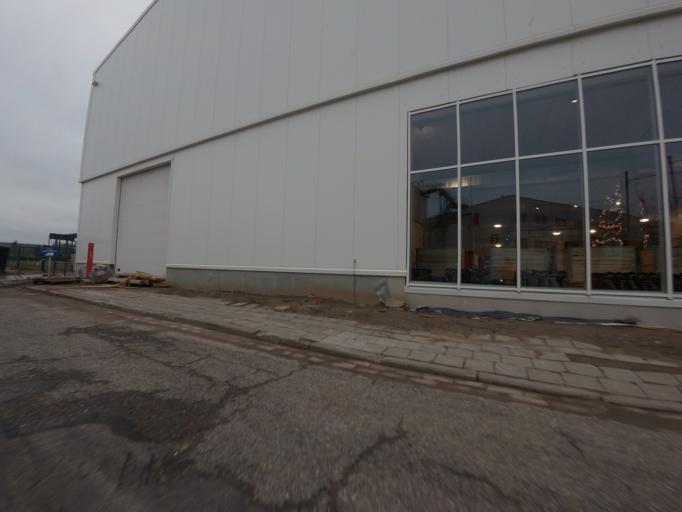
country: BE
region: Flanders
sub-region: Provincie Antwerpen
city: Aartselaar
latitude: 51.1586
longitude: 4.3748
